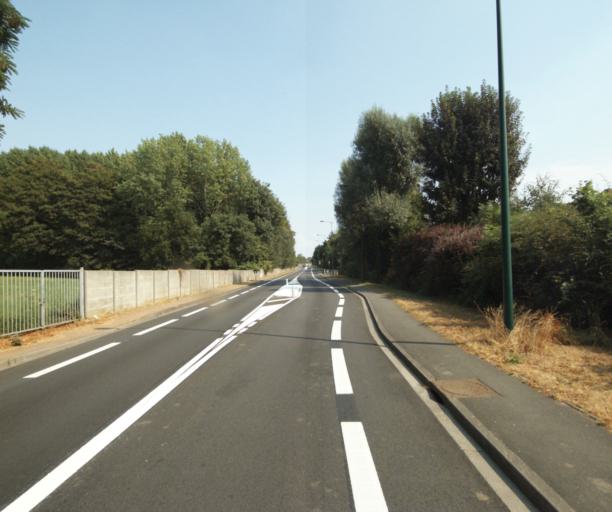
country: FR
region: Nord-Pas-de-Calais
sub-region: Departement du Nord
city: Bondues
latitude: 50.7220
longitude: 3.1045
